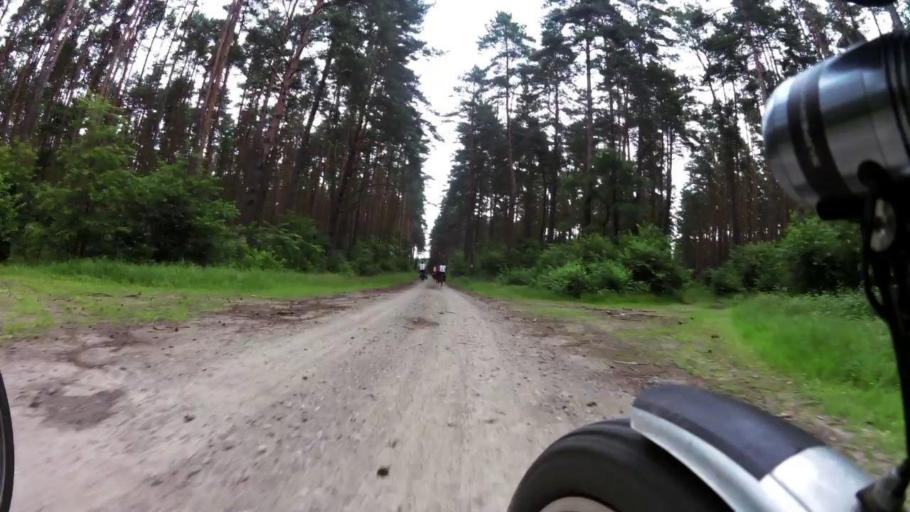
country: PL
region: West Pomeranian Voivodeship
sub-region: Powiat gryfinski
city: Mieszkowice
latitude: 52.8320
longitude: 14.5916
